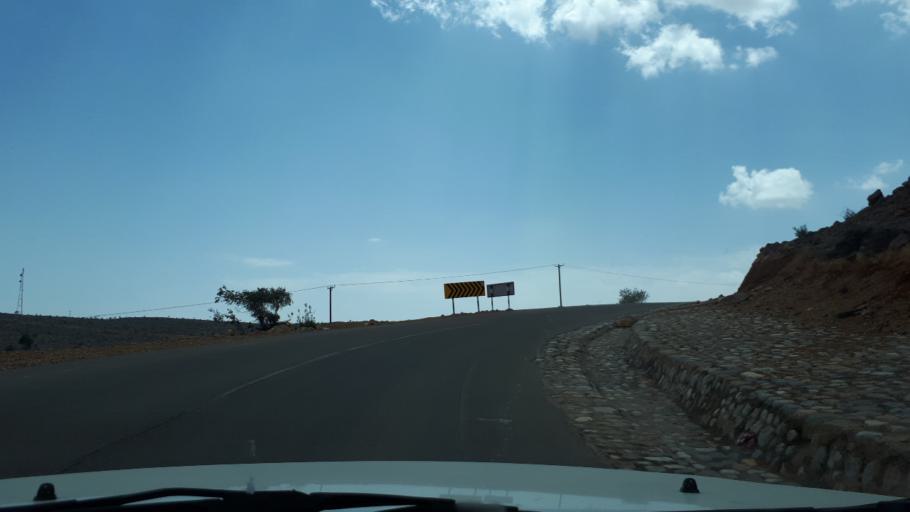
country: OM
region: Muhafazat ad Dakhiliyah
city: Bahla'
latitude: 23.2231
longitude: 57.2055
